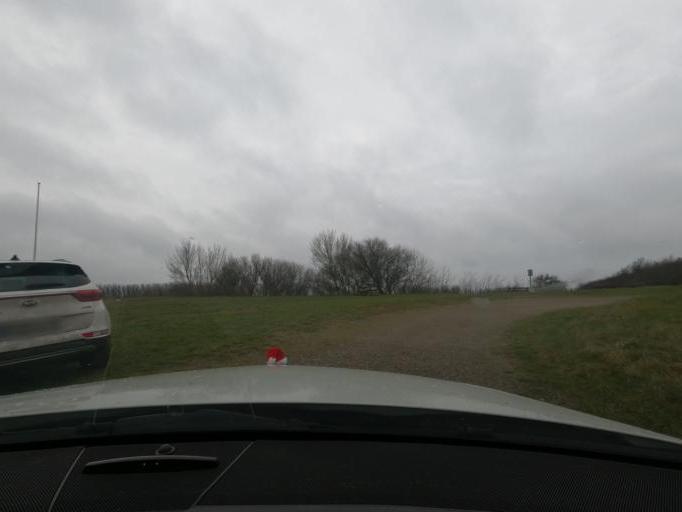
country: DK
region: South Denmark
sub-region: Haderslev Kommune
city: Starup
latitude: 55.1844
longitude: 9.6564
